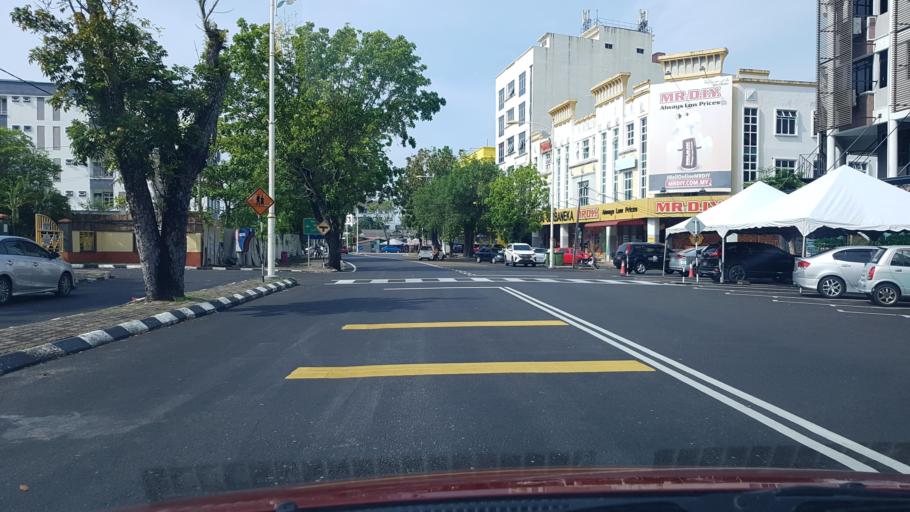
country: MY
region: Terengganu
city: Kuala Terengganu
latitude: 5.3309
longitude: 103.1423
